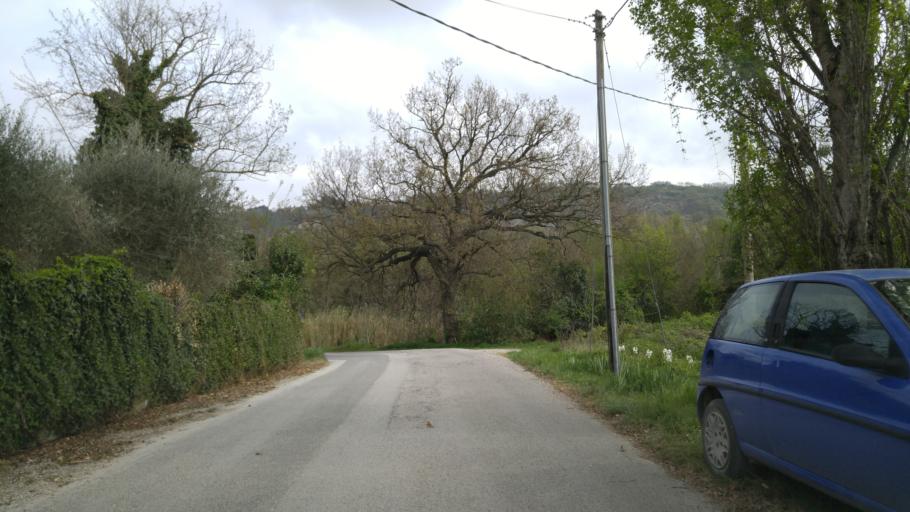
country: IT
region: The Marches
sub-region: Provincia di Pesaro e Urbino
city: Bellocchi
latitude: 43.7721
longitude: 12.9887
